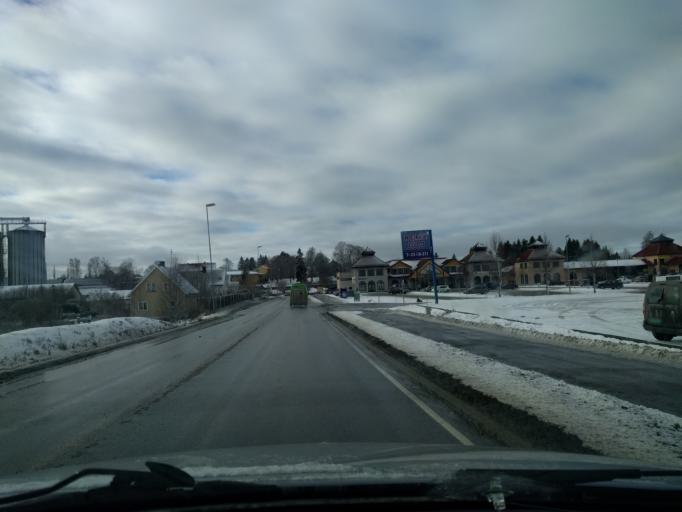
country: NO
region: Hedmark
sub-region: Stange
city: Stange
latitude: 60.7205
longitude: 11.1981
